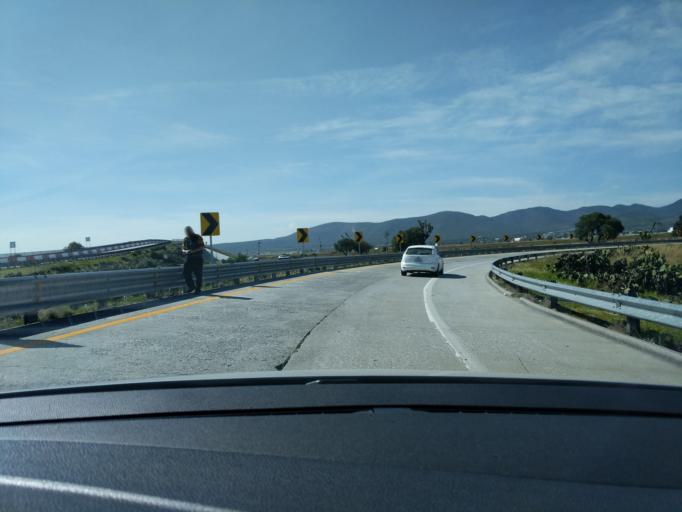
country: MX
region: Hidalgo
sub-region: Tolcayuca
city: Vicente Guerrero (San Javier)
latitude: 19.9274
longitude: -98.8933
